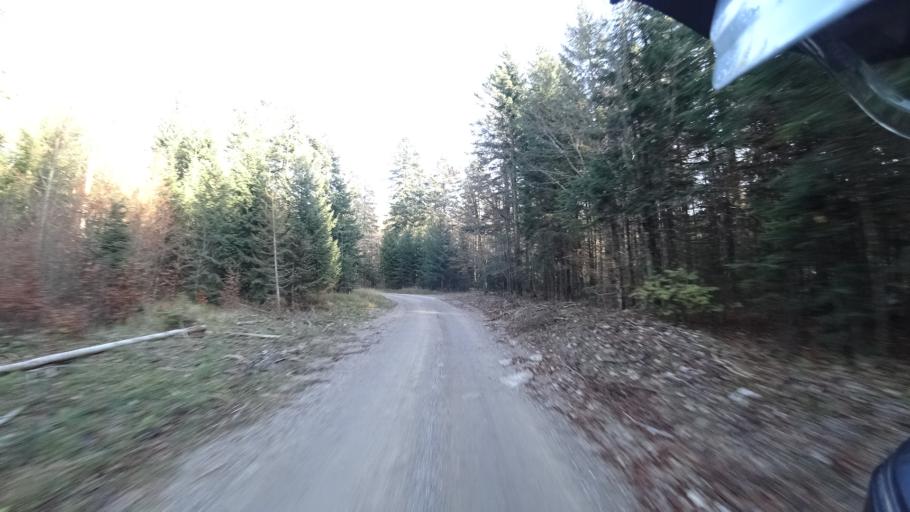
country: HR
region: Primorsko-Goranska
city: Drazice
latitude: 45.4793
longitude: 14.4755
